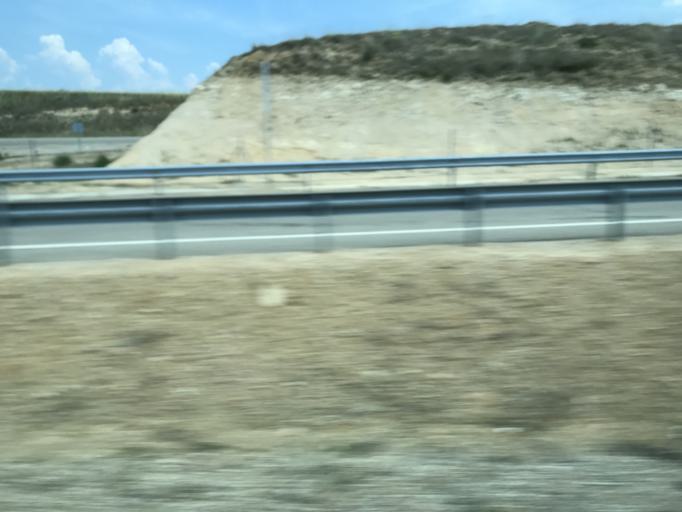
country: ES
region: Castille and Leon
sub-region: Provincia de Burgos
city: Oquillas
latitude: 41.8266
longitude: -3.7065
